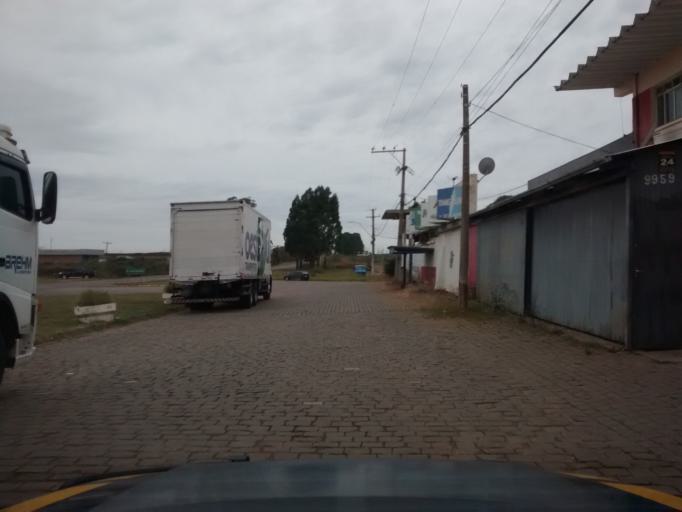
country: BR
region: Rio Grande do Sul
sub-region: Vacaria
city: Vacaria
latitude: -28.4993
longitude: -50.9179
